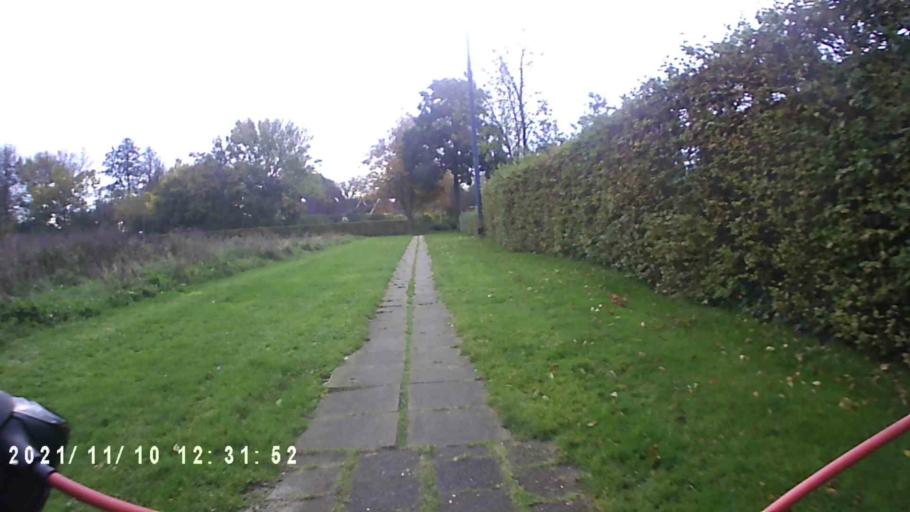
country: NL
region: Groningen
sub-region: Gemeente Groningen
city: Korrewegwijk
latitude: 53.2755
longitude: 6.5390
